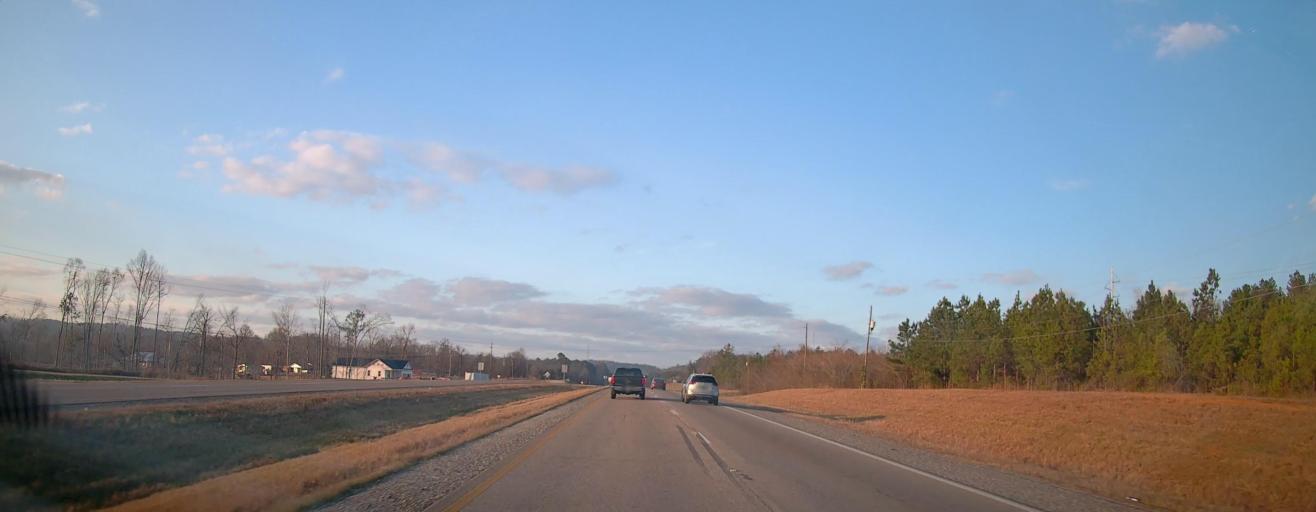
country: US
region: Alabama
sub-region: Calhoun County
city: Alexandria
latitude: 33.8205
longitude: -85.9076
